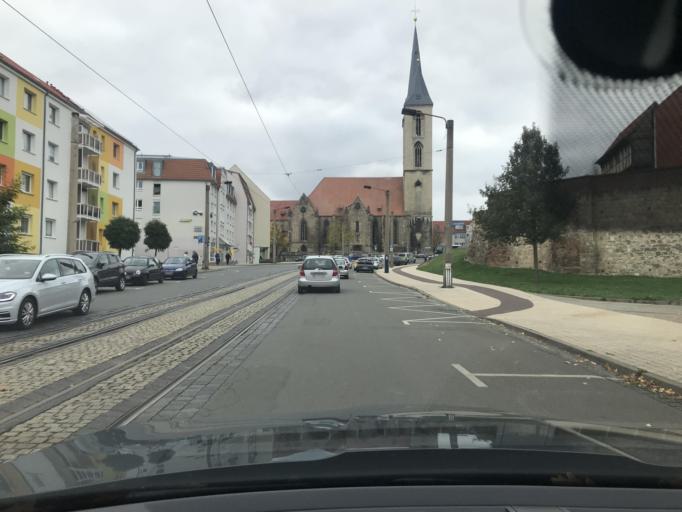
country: DE
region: Saxony-Anhalt
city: Halberstadt
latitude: 51.8972
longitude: 11.0504
